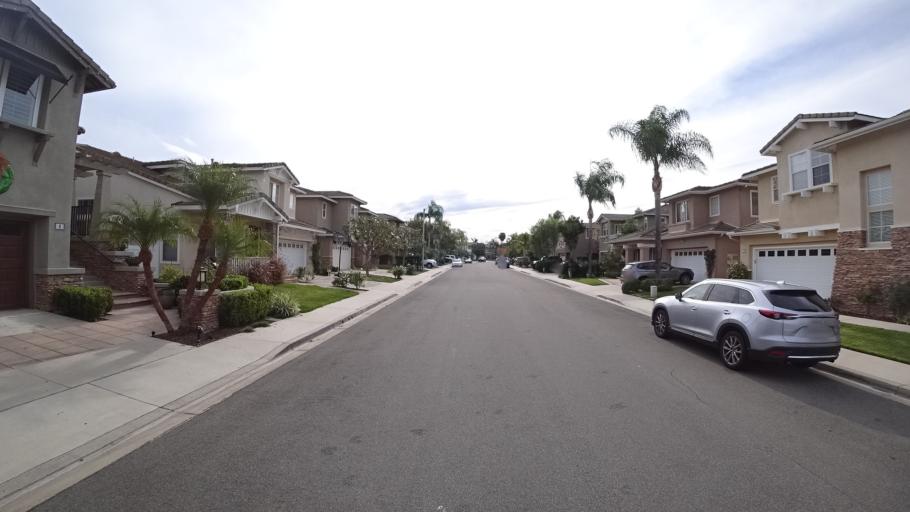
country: US
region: California
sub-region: Orange County
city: Aliso Viejo
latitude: 33.5875
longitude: -117.7453
